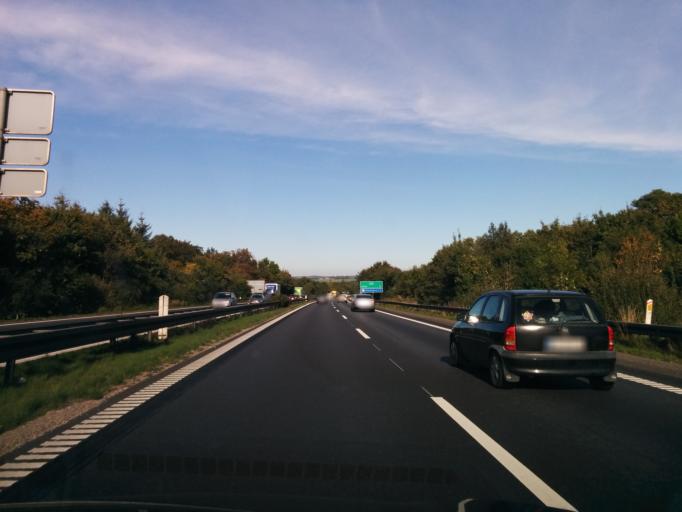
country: DK
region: Central Jutland
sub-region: Skanderborg Kommune
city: Skanderborg
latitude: 55.9917
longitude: 9.8675
